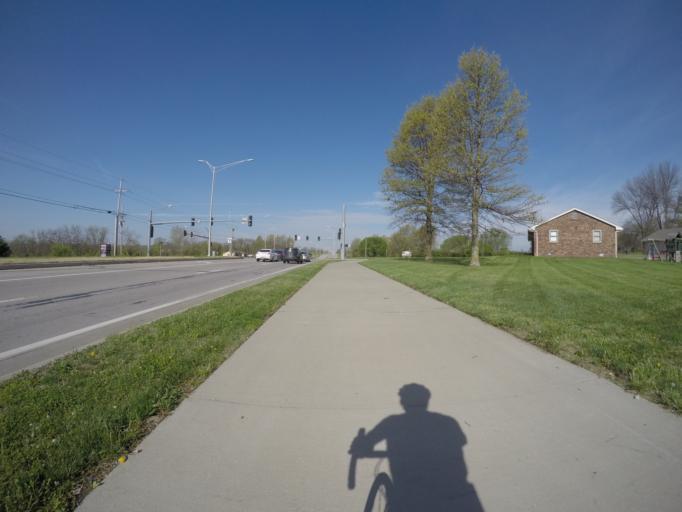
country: US
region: Missouri
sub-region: Cass County
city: Lake Winnebago
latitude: 38.8539
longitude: -94.4165
